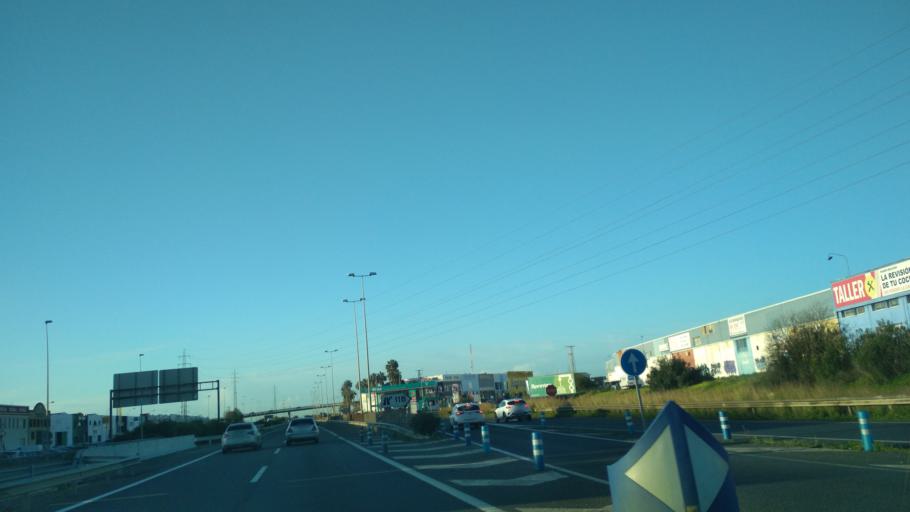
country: ES
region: Andalusia
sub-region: Provincia de Huelva
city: Huelva
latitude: 37.2654
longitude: -6.9187
